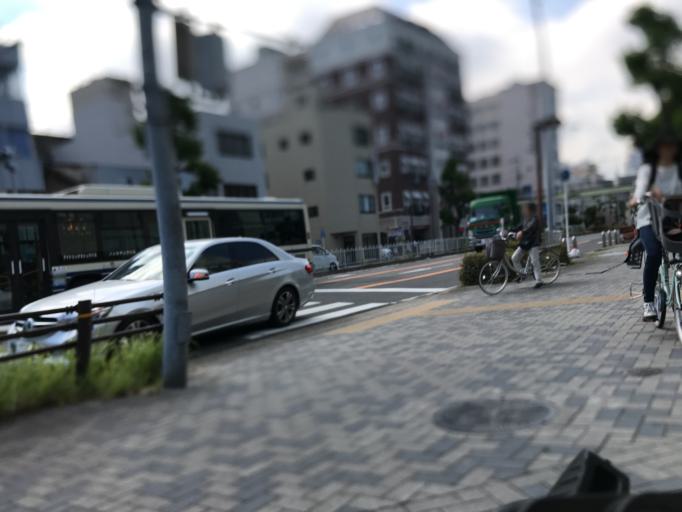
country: JP
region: Aichi
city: Nagoya-shi
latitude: 35.1778
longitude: 136.8859
